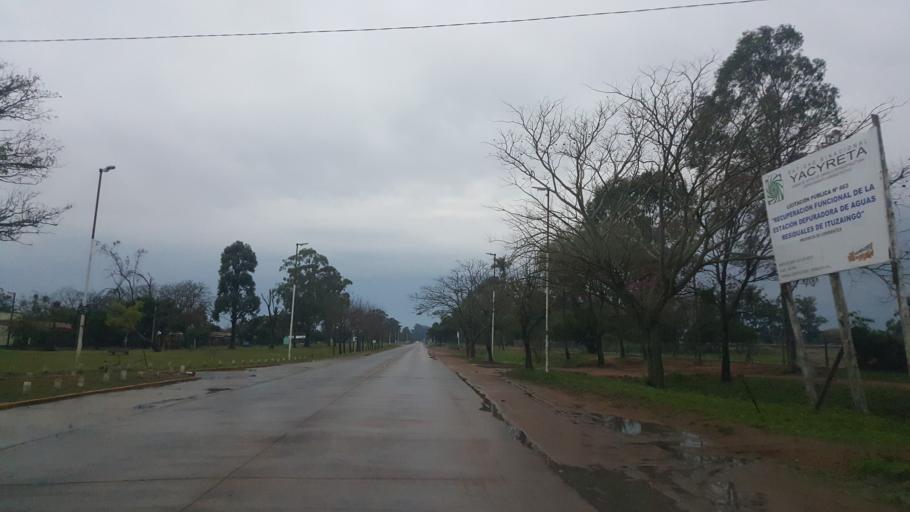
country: AR
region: Corrientes
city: Ituzaingo
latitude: -27.5903
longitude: -56.6852
